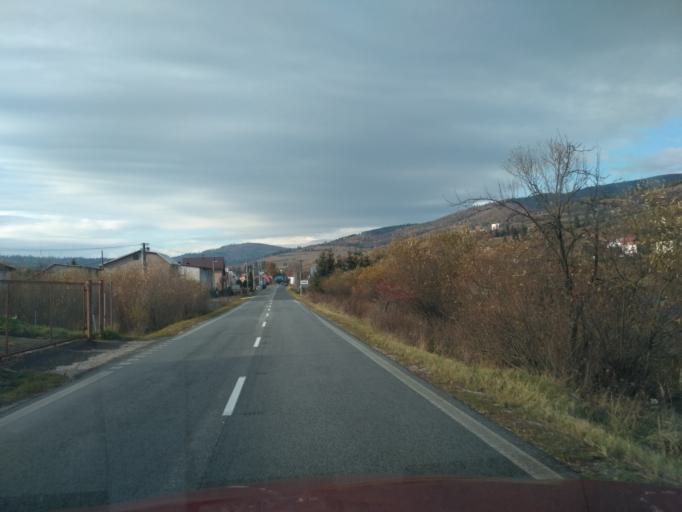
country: SK
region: Kosicky
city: Krompachy
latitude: 48.8051
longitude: 20.7276
